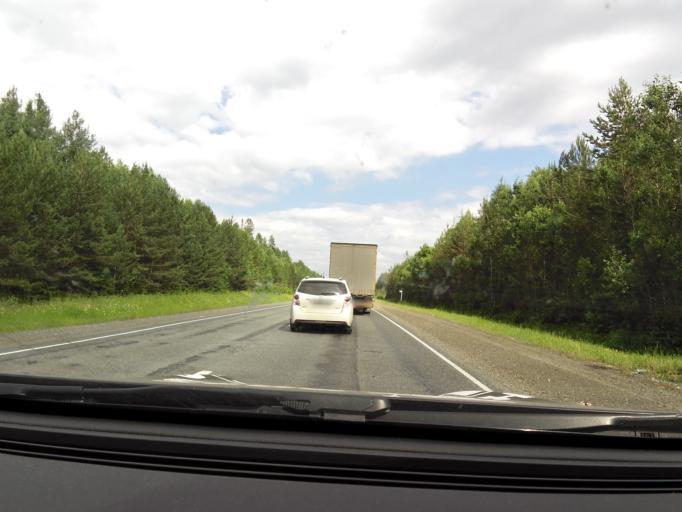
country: RU
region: Sverdlovsk
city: Nizhniye Sergi
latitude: 56.8236
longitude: 59.3077
